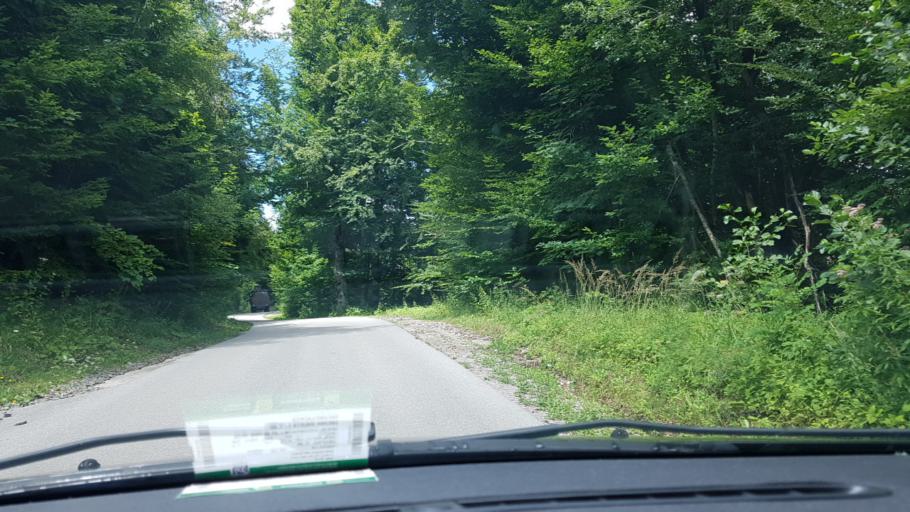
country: HR
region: Primorsko-Goranska
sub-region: Grad Delnice
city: Delnice
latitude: 45.3630
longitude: 14.7244
